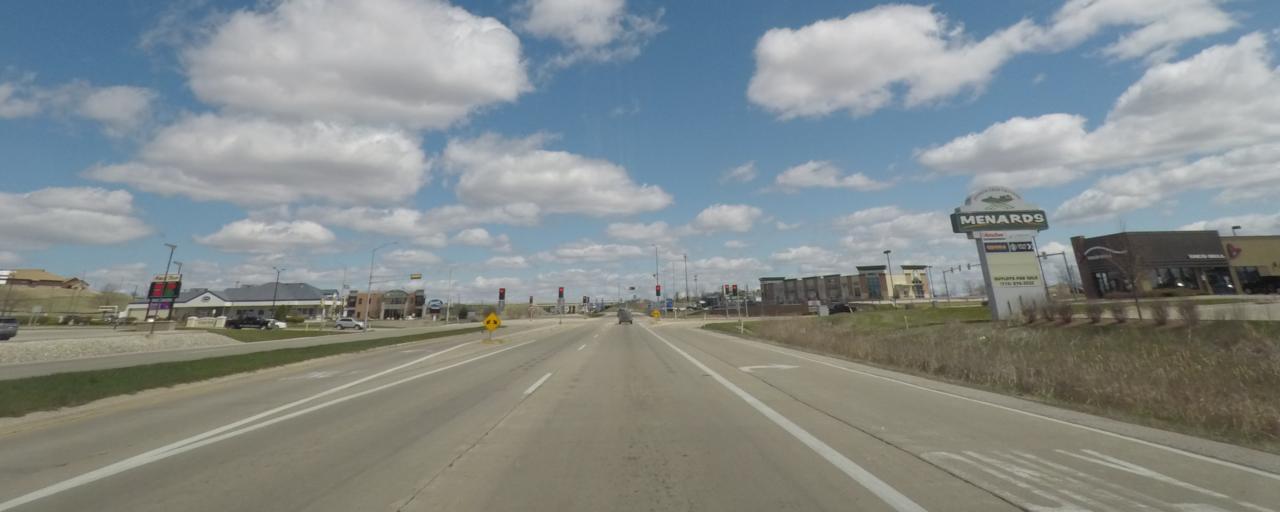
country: US
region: Wisconsin
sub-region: Jefferson County
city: Johnson Creek
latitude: 43.0817
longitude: -88.7638
